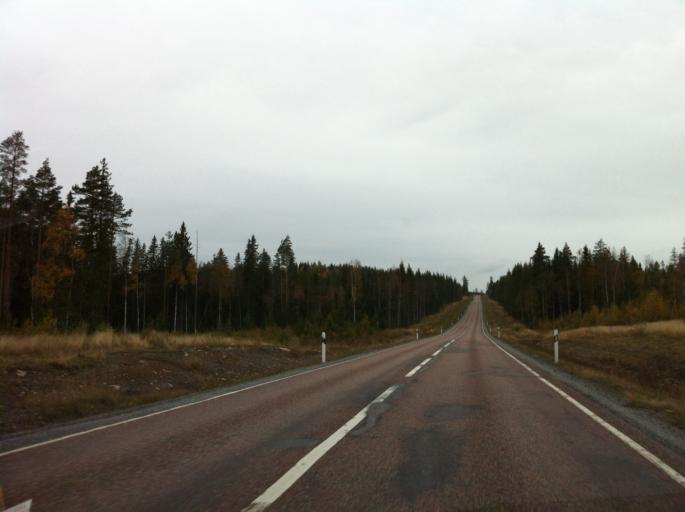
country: SE
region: Dalarna
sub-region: Ludvika Kommun
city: Grangesberg
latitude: 59.9987
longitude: 15.0088
